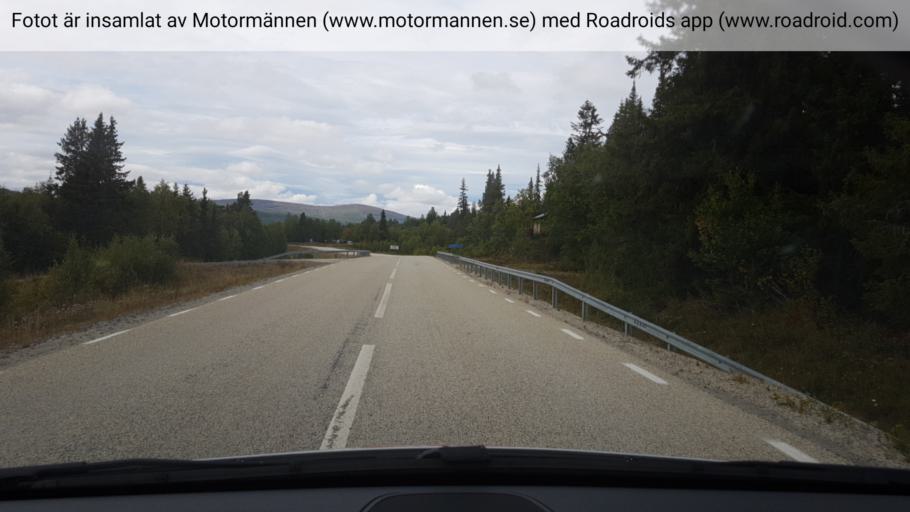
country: SE
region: Jaemtland
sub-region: Are Kommun
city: Are
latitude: 62.8490
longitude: 12.8160
